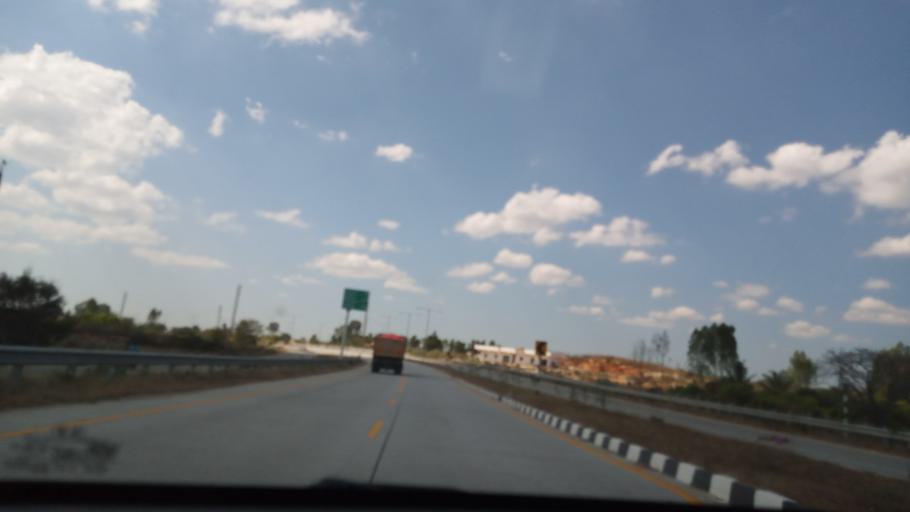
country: IN
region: Andhra Pradesh
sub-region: Chittoor
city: Palmaner
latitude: 13.2189
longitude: 78.7433
